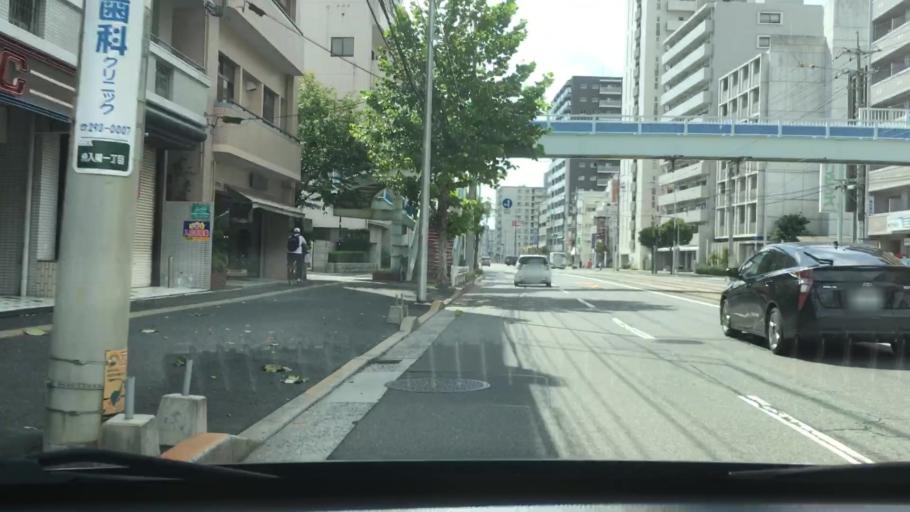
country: JP
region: Hiroshima
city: Hiroshima-shi
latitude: 34.3794
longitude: 132.4391
